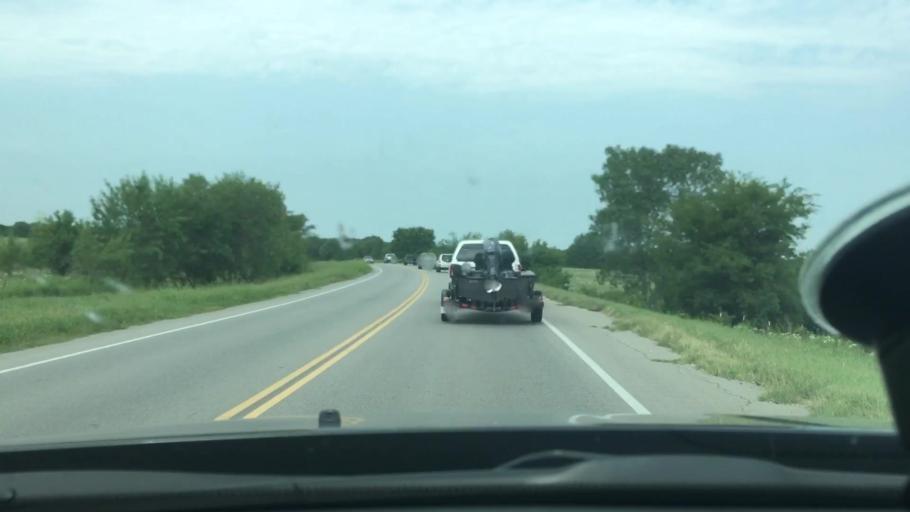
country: US
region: Oklahoma
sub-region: Marshall County
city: Madill
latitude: 34.0610
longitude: -96.7523
